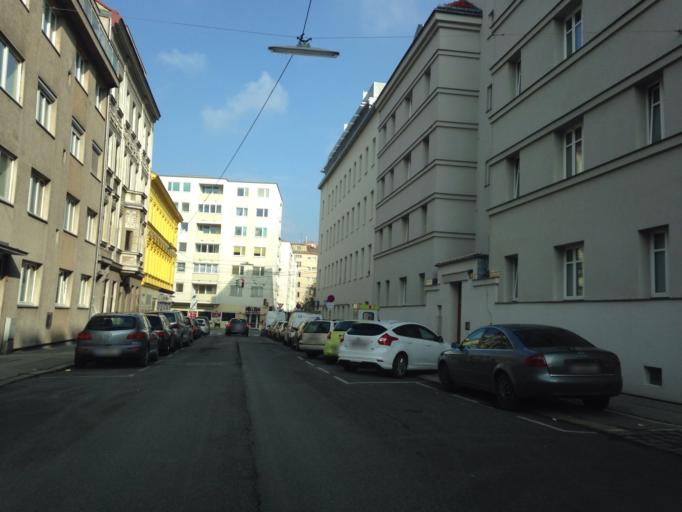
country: AT
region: Vienna
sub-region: Wien Stadt
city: Vienna
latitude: 48.2113
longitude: 16.3154
